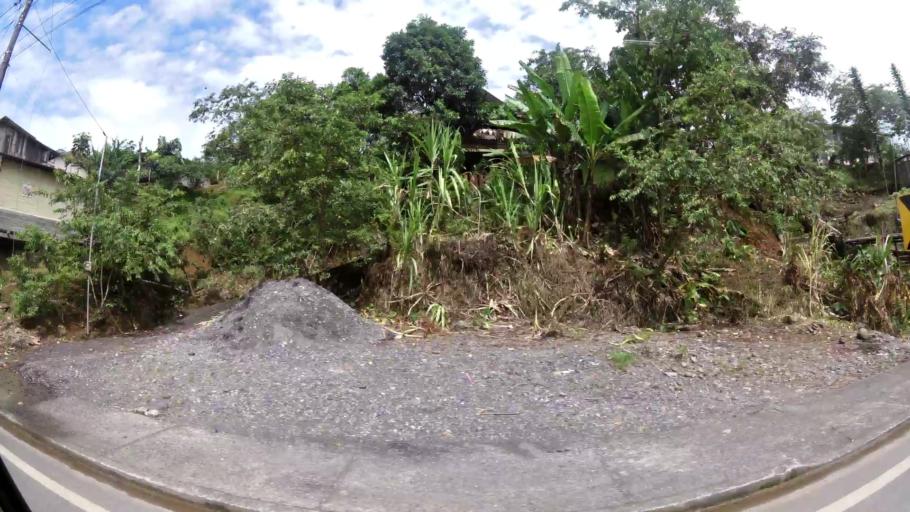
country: EC
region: Pastaza
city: Puyo
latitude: -1.4958
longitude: -78.0204
